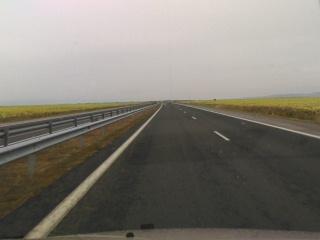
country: BG
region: Stara Zagora
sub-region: Obshtina Radnevo
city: Radnevo
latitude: 42.3991
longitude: 25.9028
